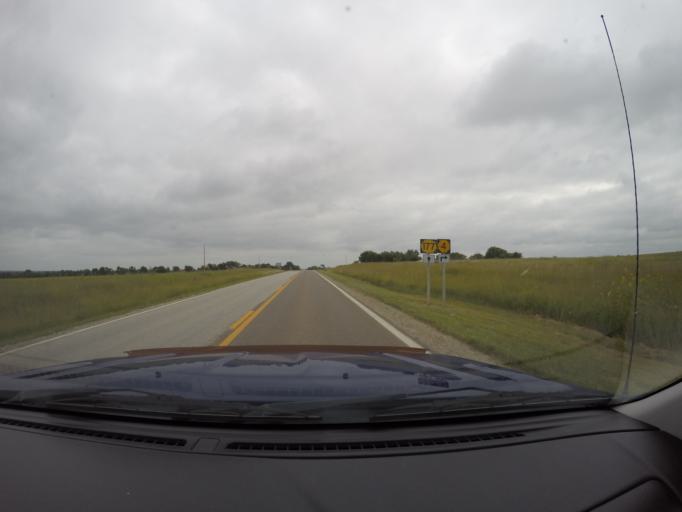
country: US
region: Kansas
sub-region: Morris County
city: Council Grove
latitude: 38.8431
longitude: -96.5015
